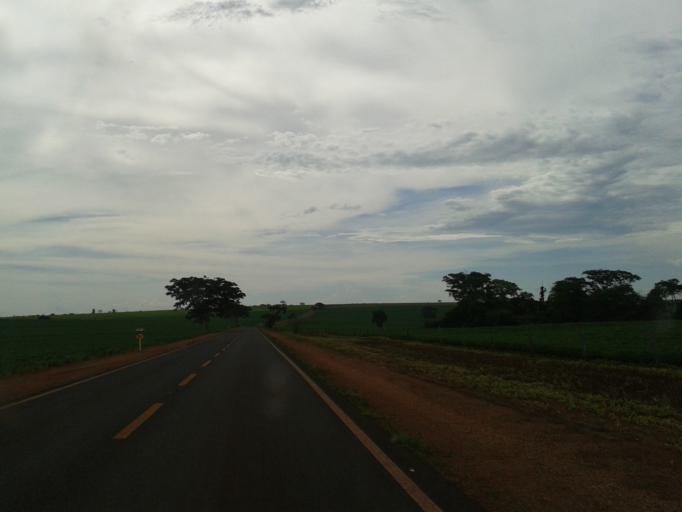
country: BR
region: Minas Gerais
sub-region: Capinopolis
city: Capinopolis
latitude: -18.6930
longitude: -49.4826
